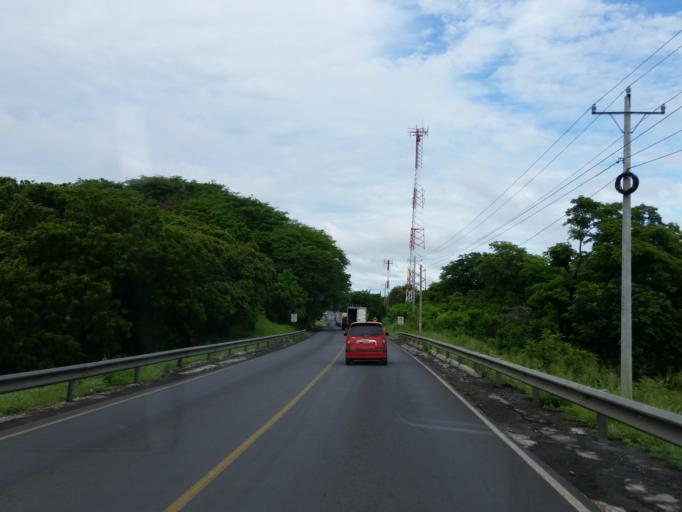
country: NI
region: Leon
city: Nagarote
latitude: 12.2766
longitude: -86.4983
